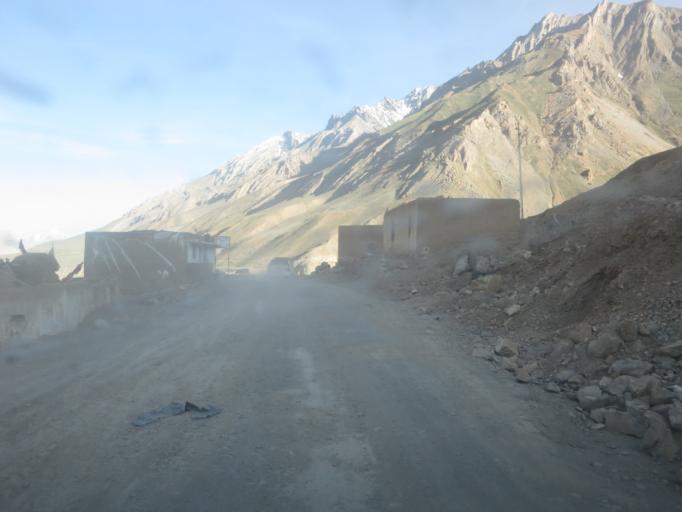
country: IN
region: Himachal Pradesh
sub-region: Kulu
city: Manali
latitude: 32.3338
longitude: 77.9254
